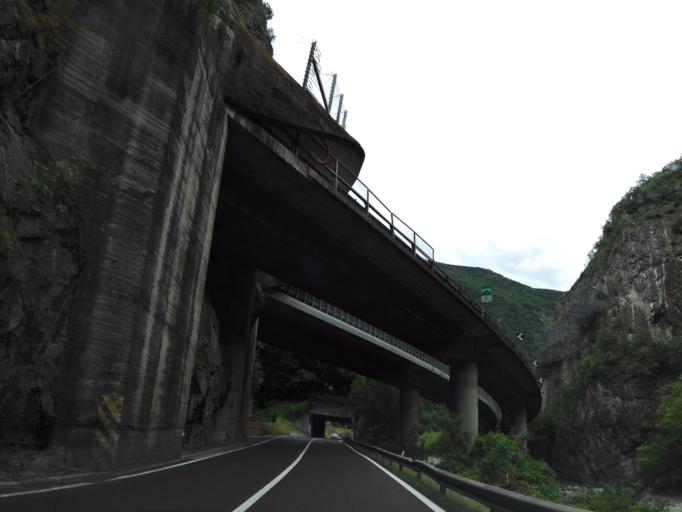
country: IT
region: Trentino-Alto Adige
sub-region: Bolzano
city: Cornedo All'Isarco
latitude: 46.4929
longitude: 11.4316
